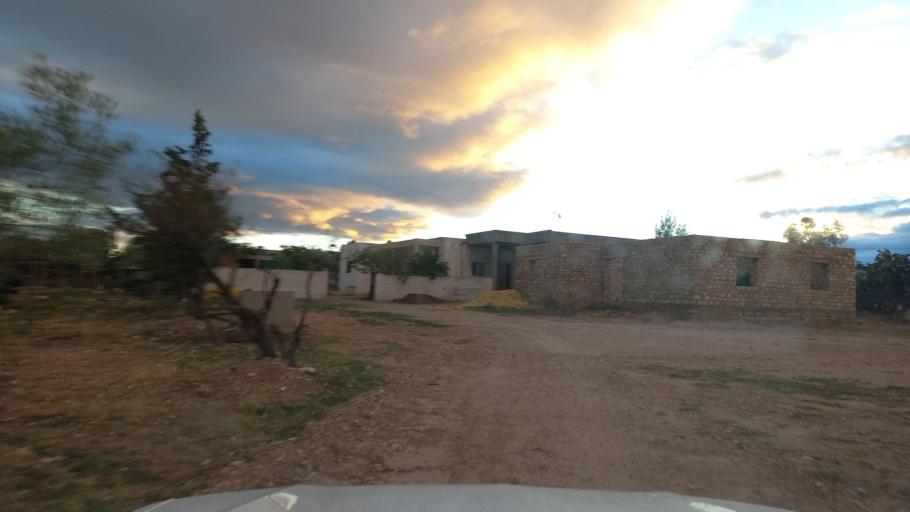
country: TN
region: Al Qasrayn
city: Kasserine
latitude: 35.2603
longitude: 8.9376
